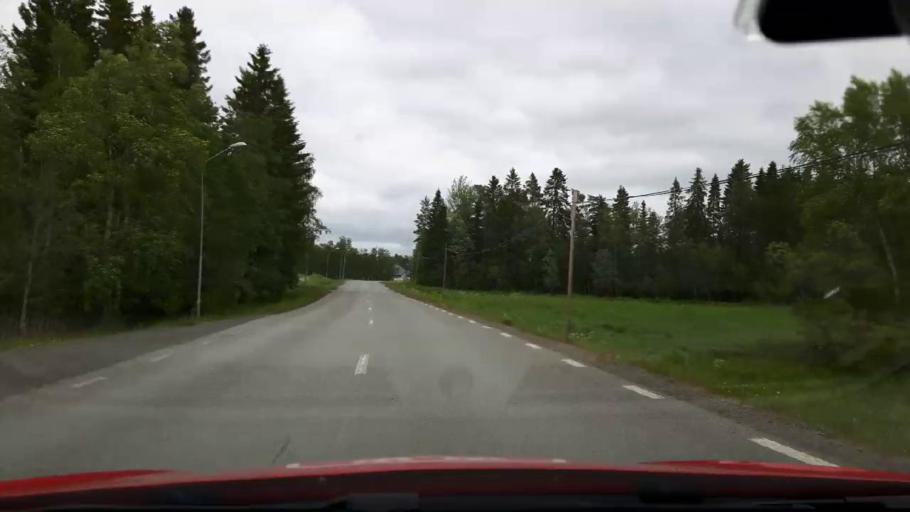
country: SE
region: Jaemtland
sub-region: OEstersunds Kommun
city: Lit
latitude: 63.6710
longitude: 15.0862
